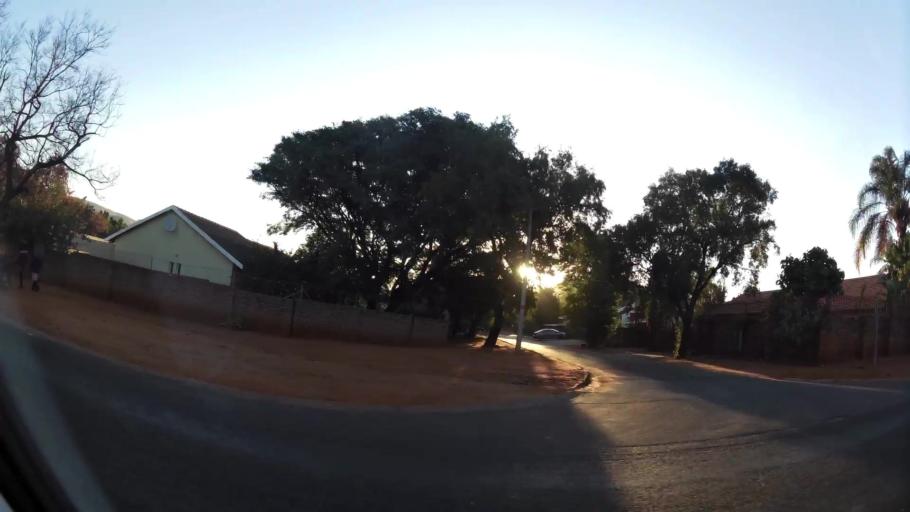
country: ZA
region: North-West
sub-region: Bojanala Platinum District Municipality
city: Rustenburg
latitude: -25.6992
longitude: 27.2356
